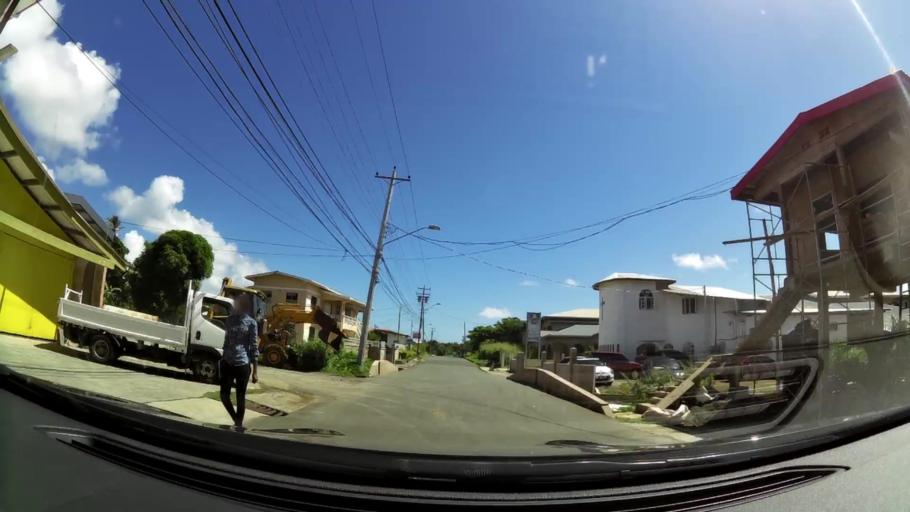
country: TT
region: Tobago
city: Scarborough
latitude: 11.1694
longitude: -60.7923
